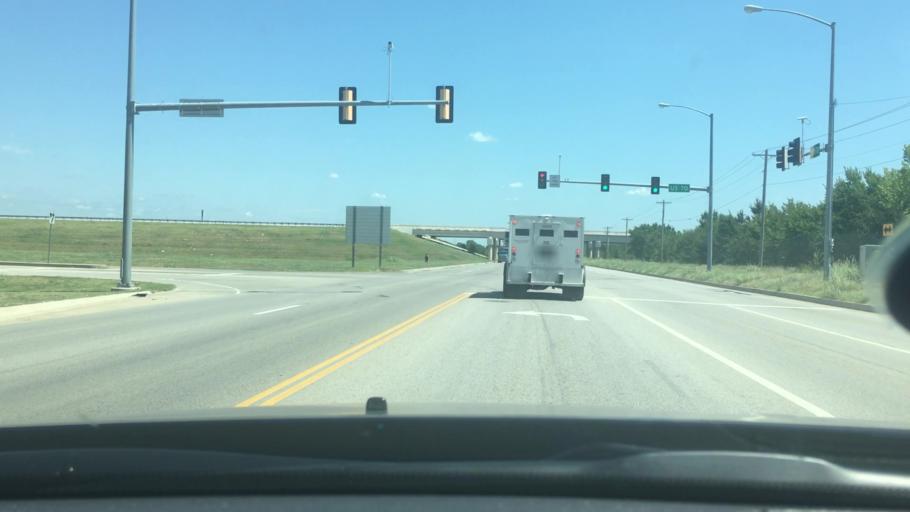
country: US
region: Oklahoma
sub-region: Bryan County
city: Durant
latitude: 33.9632
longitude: -96.3978
